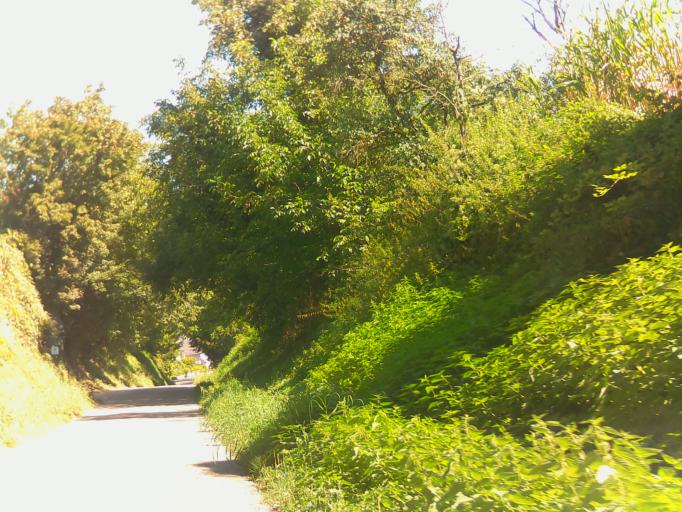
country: DE
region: Baden-Wuerttemberg
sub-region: Karlsruhe Region
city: Ubstadt-Weiher
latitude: 49.1373
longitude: 8.6604
